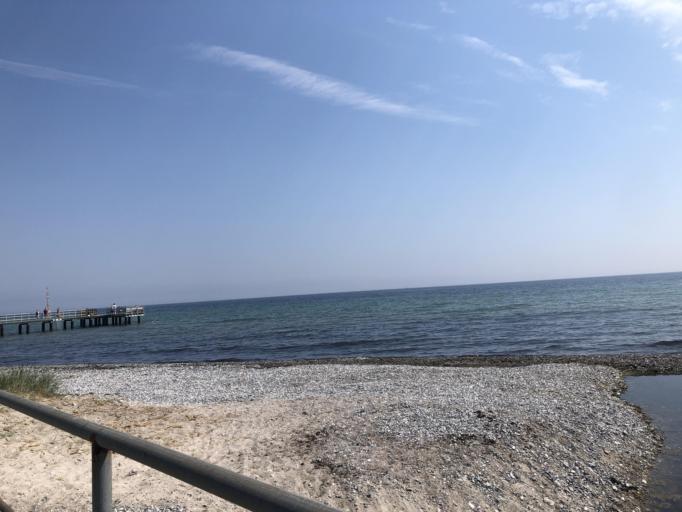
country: SE
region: Skane
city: Smygehamn
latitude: 55.3485
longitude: 13.3863
